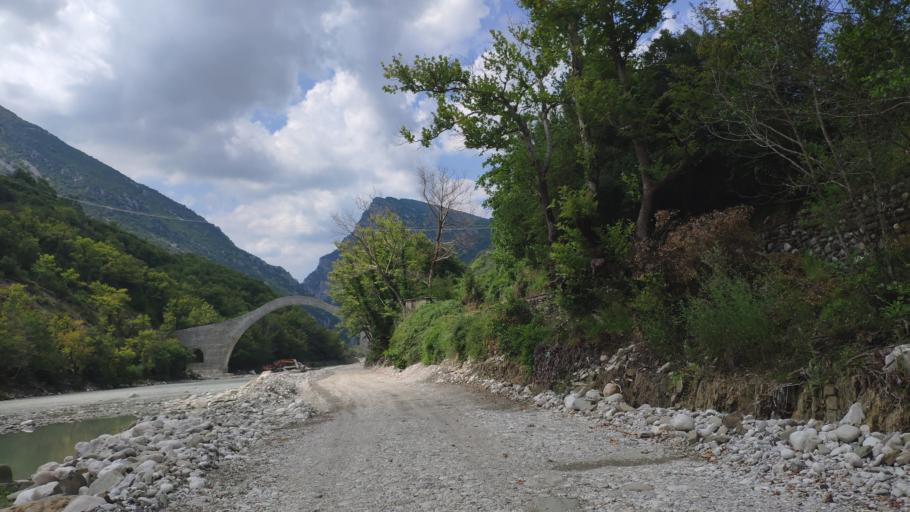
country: GR
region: Epirus
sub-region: Nomos Artas
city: Agios Dimitrios
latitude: 39.4590
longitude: 21.0313
